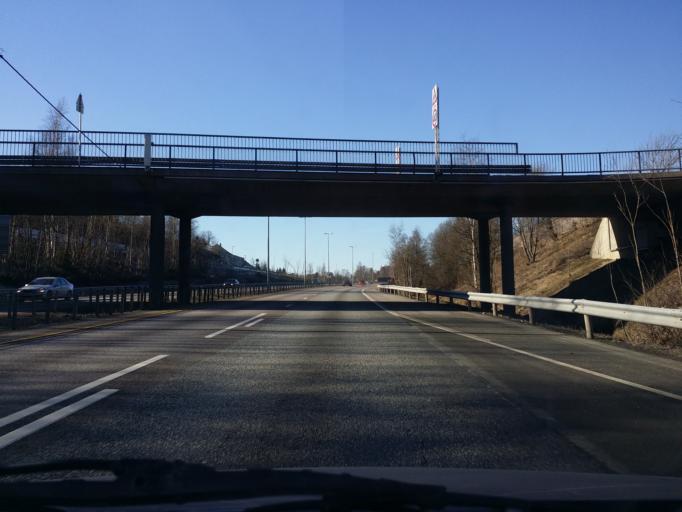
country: NO
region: Akershus
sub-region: Asker
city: Asker
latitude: 59.8290
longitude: 10.4068
